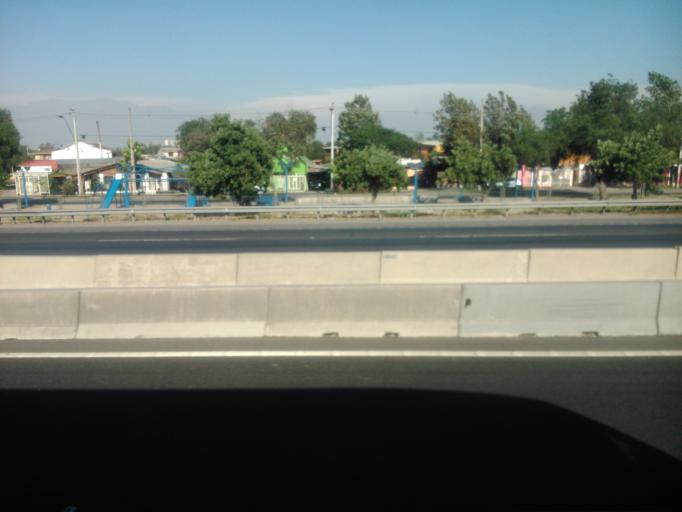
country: CL
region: Santiago Metropolitan
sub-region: Provincia de Maipo
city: San Bernardo
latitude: -33.5798
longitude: -70.7137
